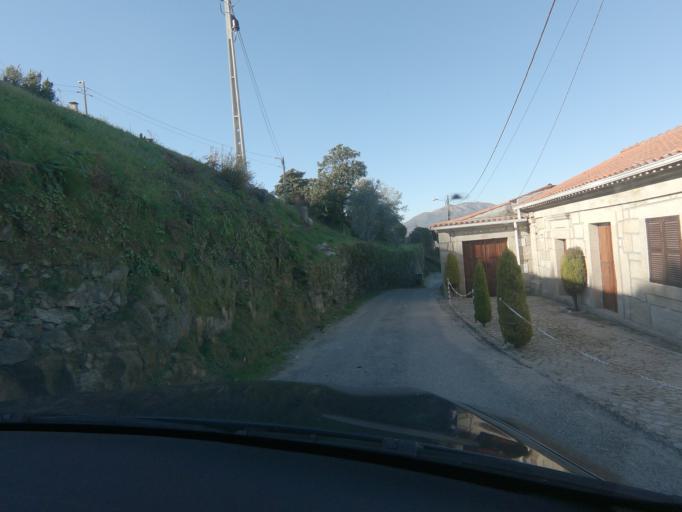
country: PT
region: Viseu
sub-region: Oliveira de Frades
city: Oliveira de Frades
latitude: 40.7312
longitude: -8.1572
